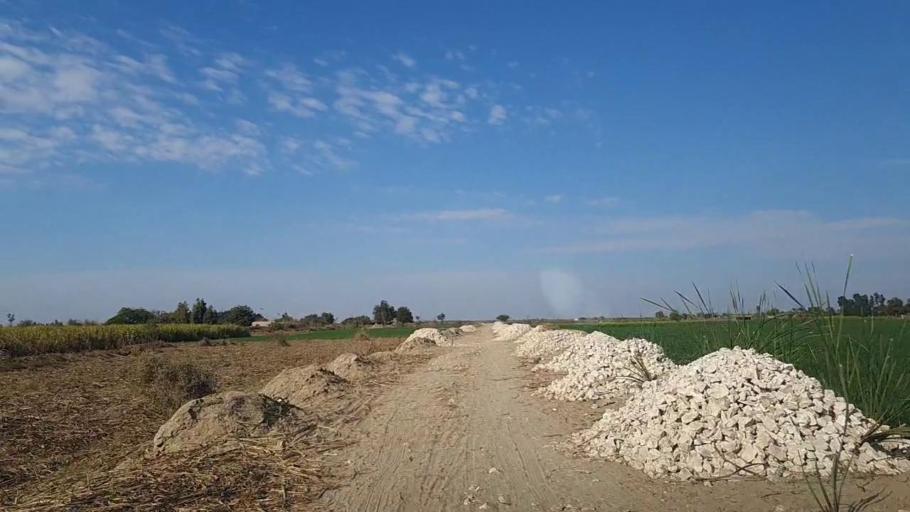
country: PK
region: Sindh
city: Jam Sahib
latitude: 26.3140
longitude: 68.8081
